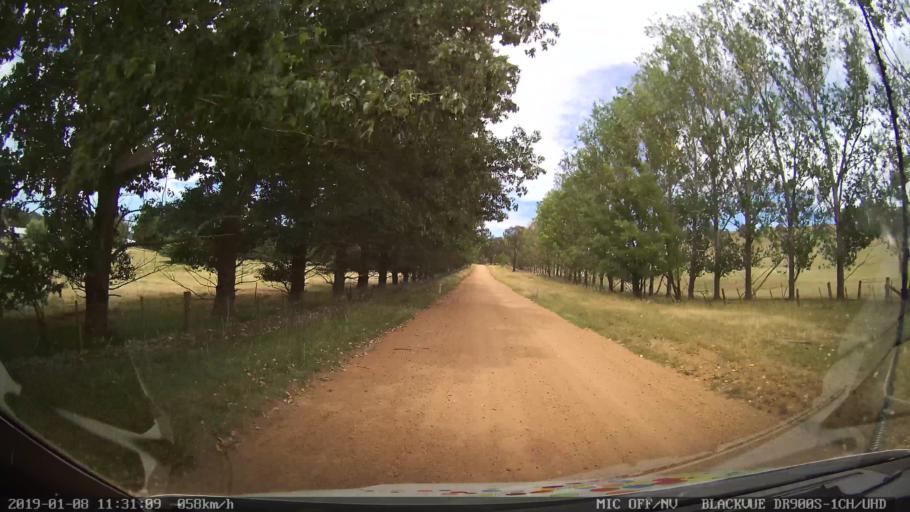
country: AU
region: New South Wales
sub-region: Guyra
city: Guyra
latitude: -30.3111
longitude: 151.5396
